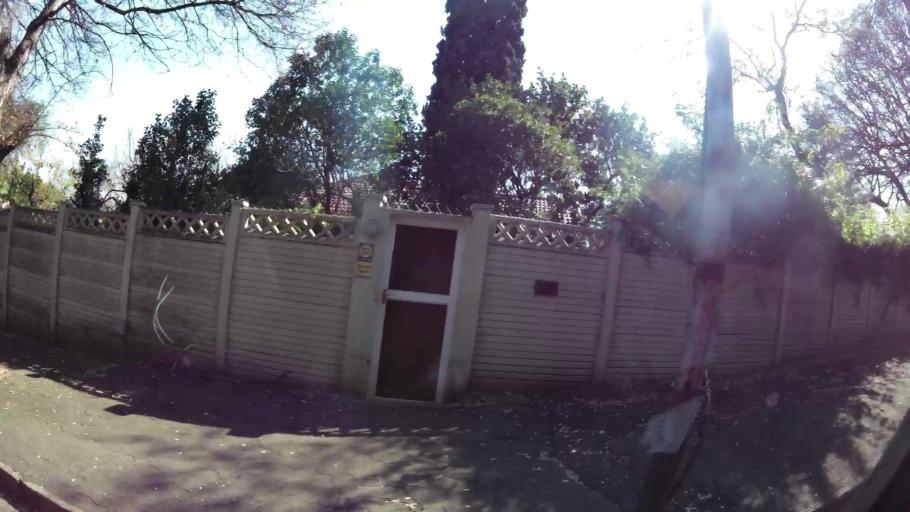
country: ZA
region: Gauteng
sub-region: City of Johannesburg Metropolitan Municipality
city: Johannesburg
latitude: -26.1536
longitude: 28.0282
